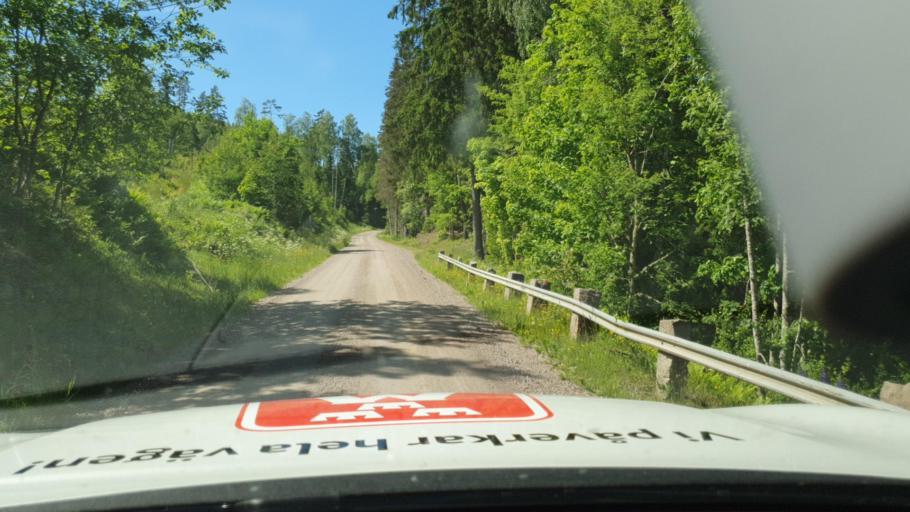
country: SE
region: Joenkoeping
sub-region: Mullsjo Kommun
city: Mullsjoe
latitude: 58.0393
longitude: 13.8634
